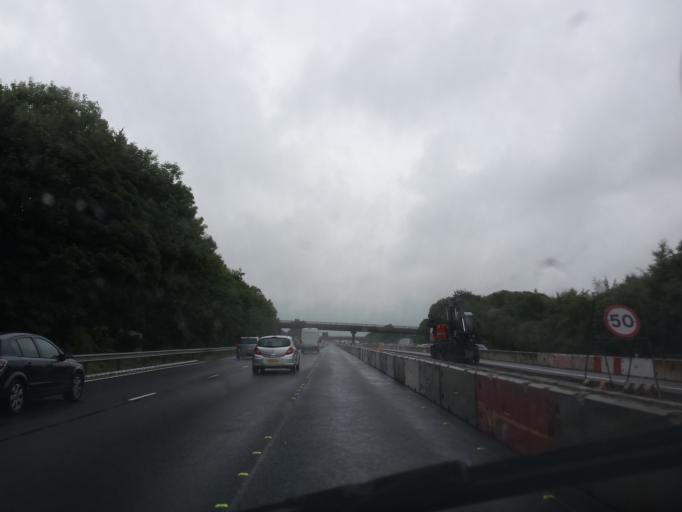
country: GB
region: England
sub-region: Derbyshire
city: Barlborough
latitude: 53.2915
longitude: -1.2939
